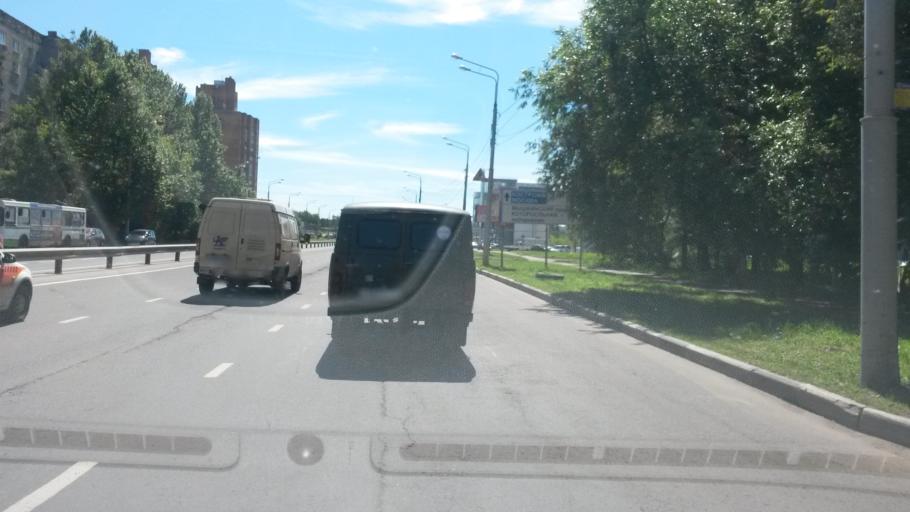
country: RU
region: Jaroslavl
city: Yaroslavl
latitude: 57.6203
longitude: 39.8581
